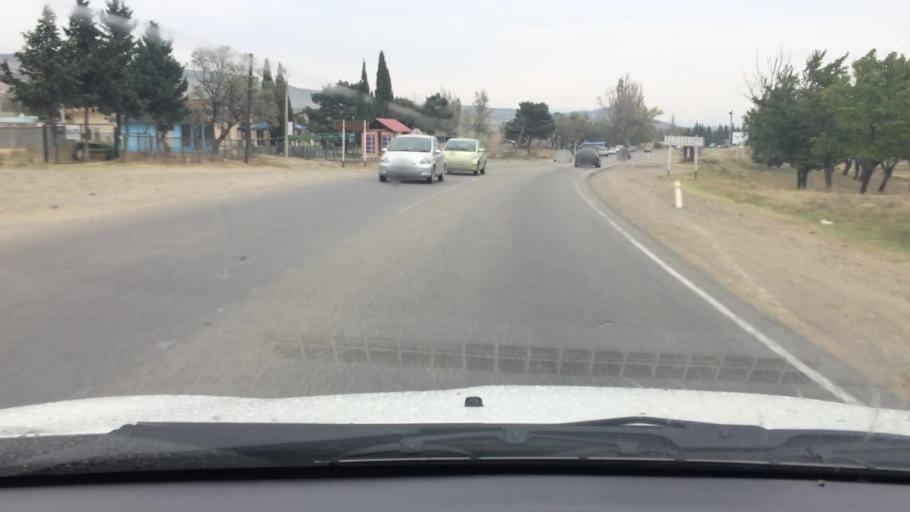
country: GE
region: T'bilisi
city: Tbilisi
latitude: 41.6290
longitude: 44.8083
